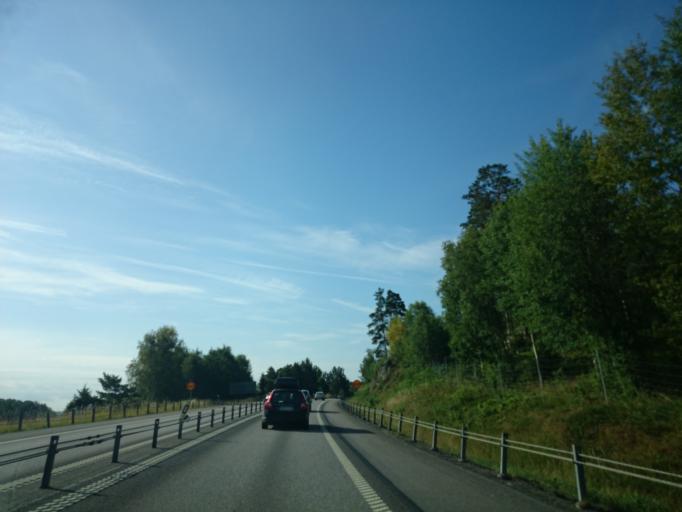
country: SE
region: OEstergoetland
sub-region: Soderkopings Kommun
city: Soederkoeping
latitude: 58.3962
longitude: 16.4094
